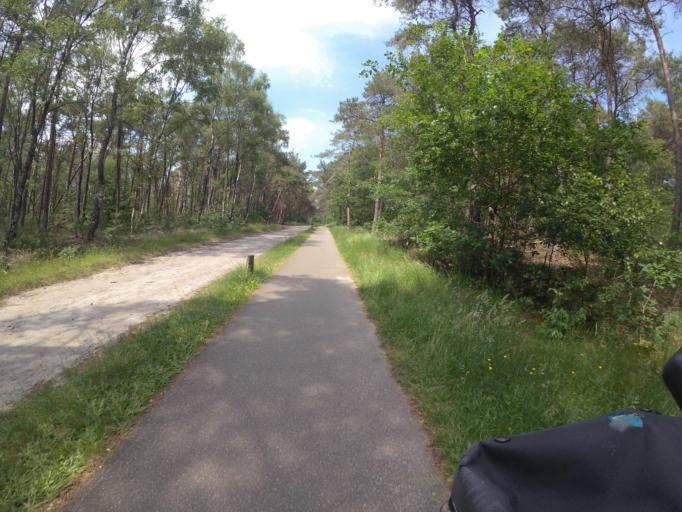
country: NL
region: Overijssel
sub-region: Gemeente Twenterand
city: Den Ham
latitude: 52.3807
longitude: 6.4337
